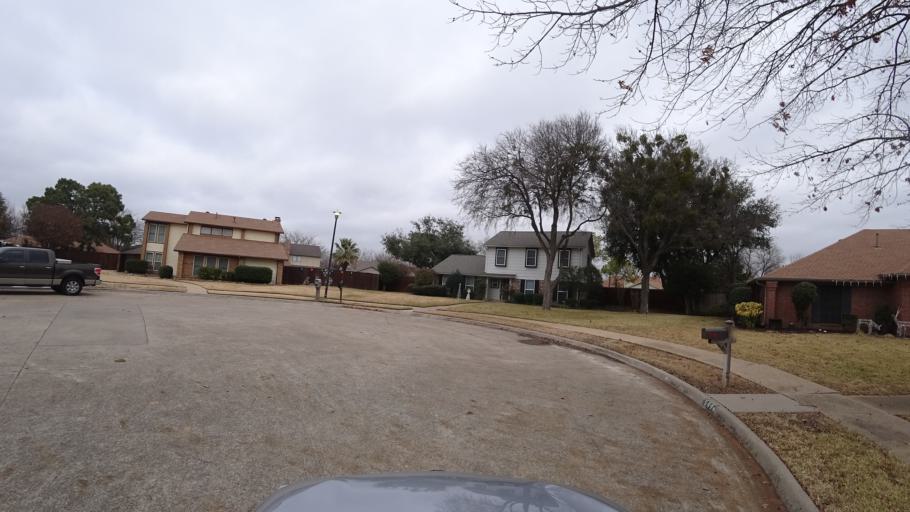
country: US
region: Texas
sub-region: Denton County
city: Highland Village
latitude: 33.0483
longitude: -97.0414
